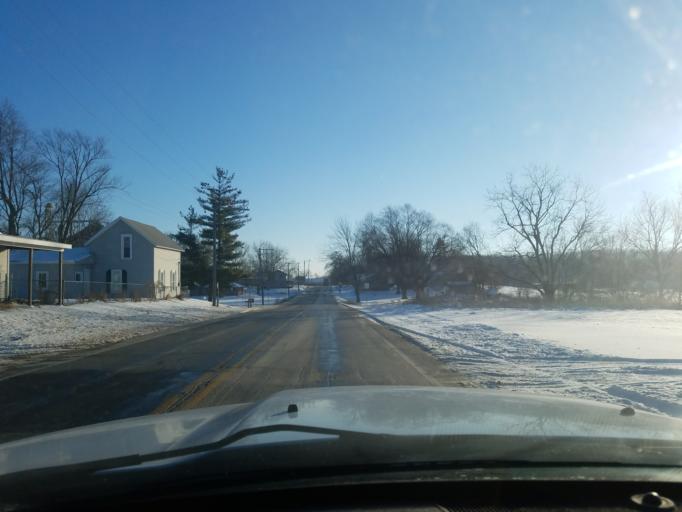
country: US
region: Indiana
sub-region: Noble County
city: Albion
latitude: 41.4569
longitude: -85.4855
